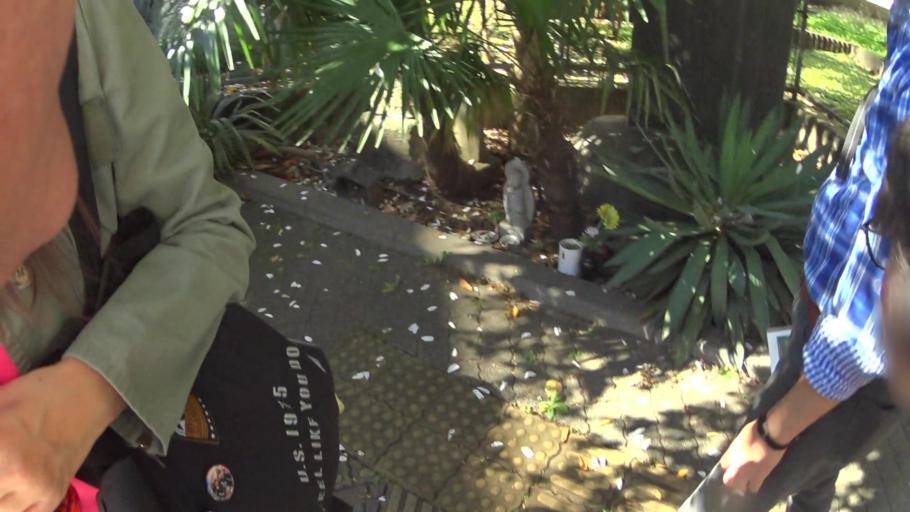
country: JP
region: Tokyo
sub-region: Machida-shi
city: Machida
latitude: 35.5482
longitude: 139.4473
